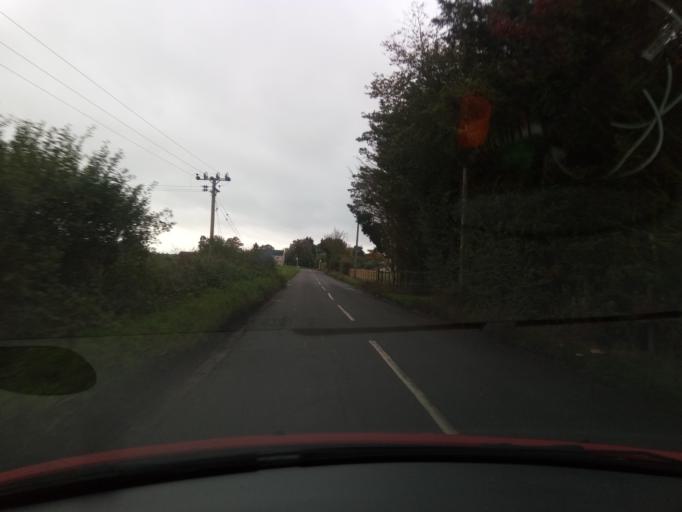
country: GB
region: England
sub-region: Essex
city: West Mersea
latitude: 51.7865
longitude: 0.9393
